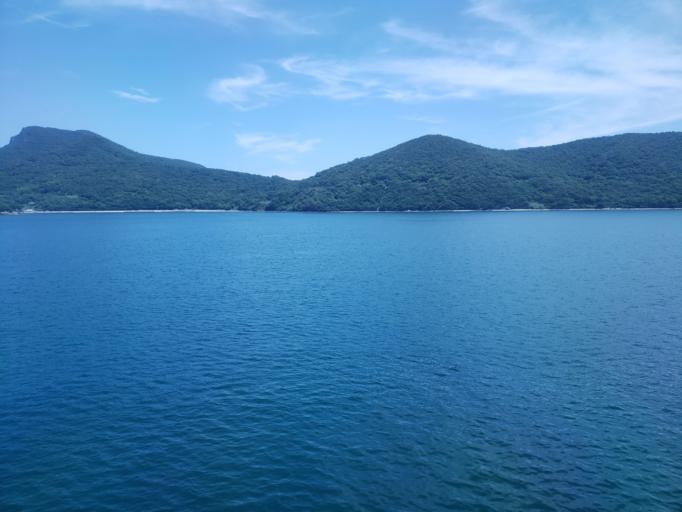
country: JP
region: Kagawa
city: Tonosho
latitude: 34.4370
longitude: 134.3200
